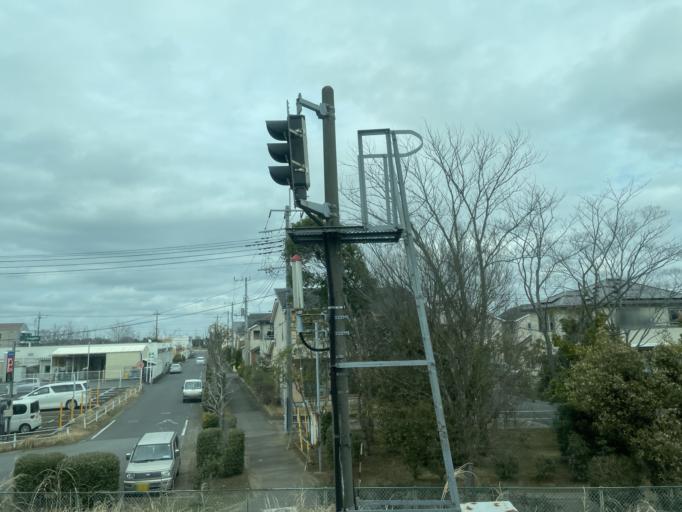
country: JP
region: Ibaraki
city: Ryugasaki
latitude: 35.8301
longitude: 140.1943
